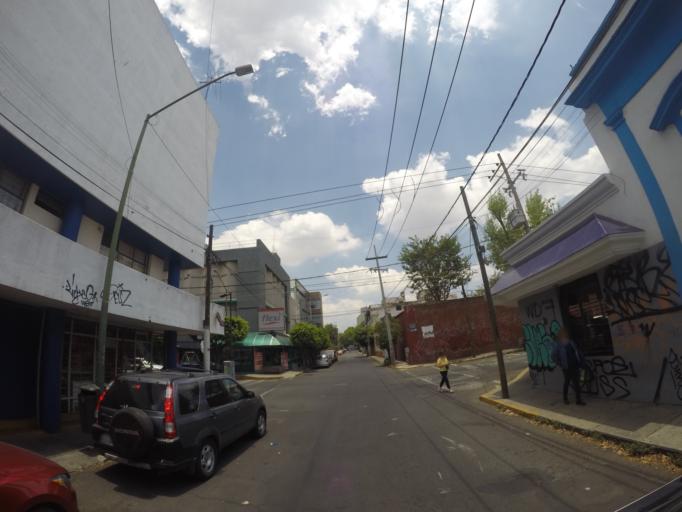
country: MX
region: Jalisco
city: Guadalajara
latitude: 20.6762
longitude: -103.3619
